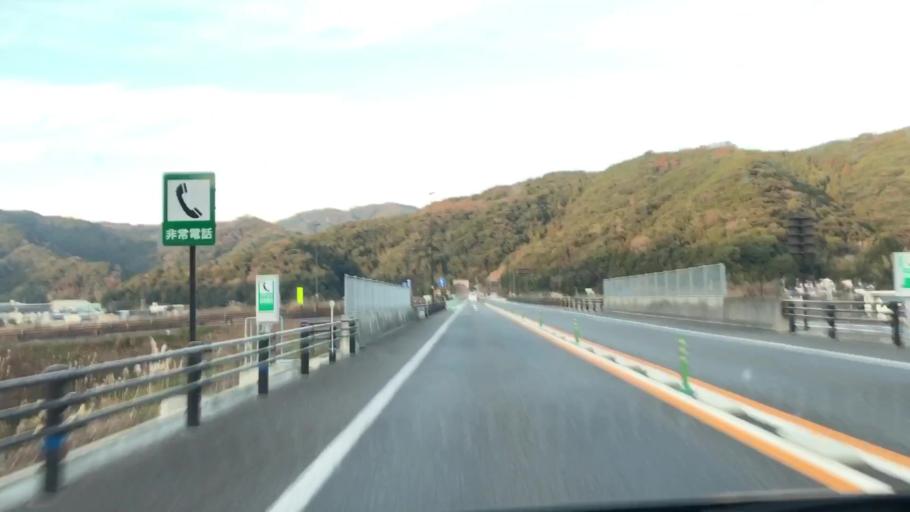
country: JP
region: Kumamoto
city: Minamata
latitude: 32.2974
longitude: 130.5088
